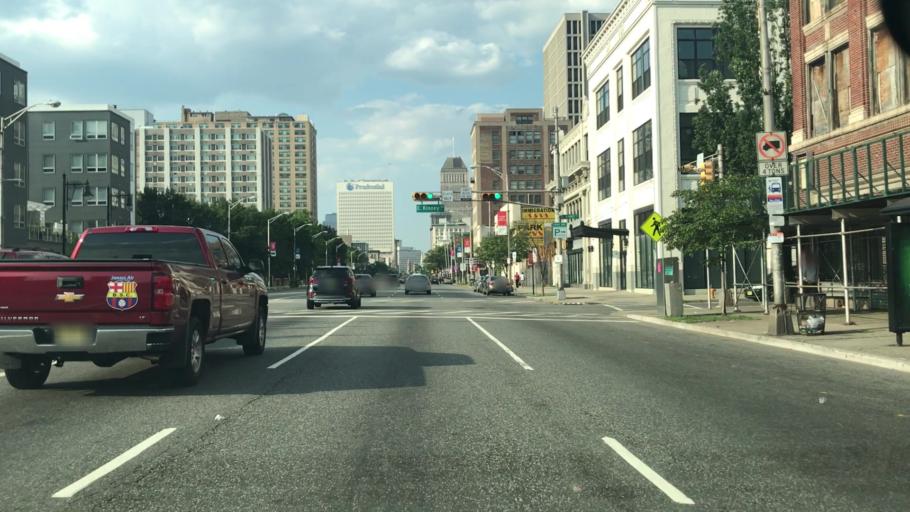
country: US
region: New Jersey
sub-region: Essex County
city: Newark
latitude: 40.7285
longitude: -74.1761
